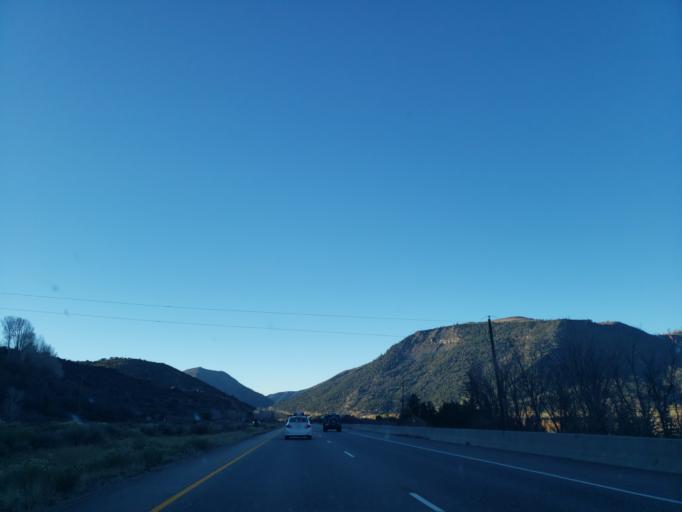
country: US
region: Colorado
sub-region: Pitkin County
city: Snowmass Village
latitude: 39.2790
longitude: -106.8971
